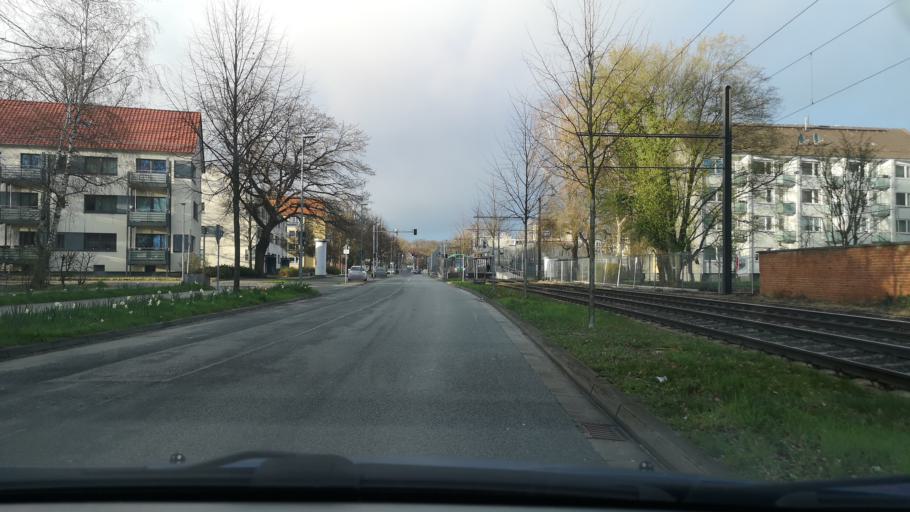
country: DE
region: Lower Saxony
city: Auf der Horst
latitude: 52.4081
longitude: 9.6619
